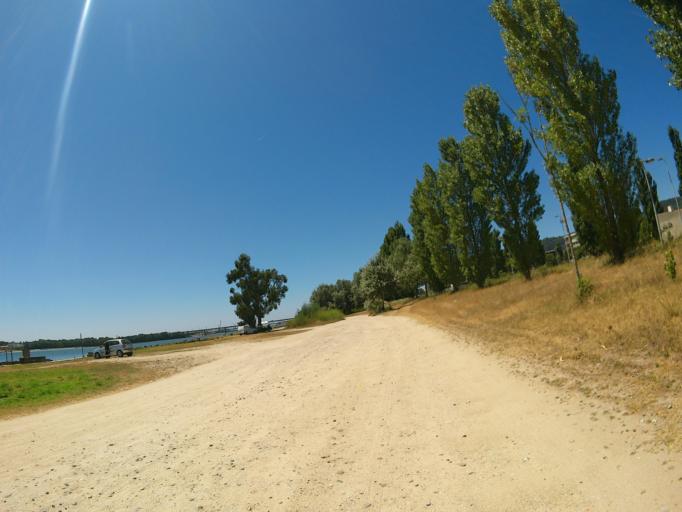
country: PT
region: Viana do Castelo
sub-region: Viana do Castelo
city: Meadela
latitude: 41.6972
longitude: -8.8073
